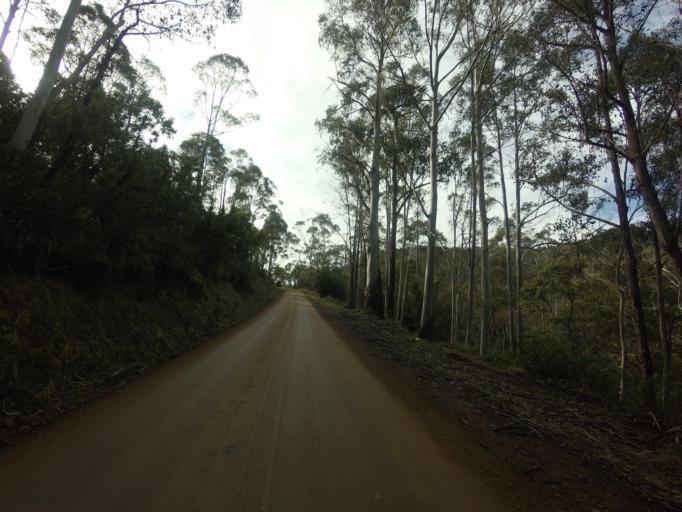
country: AU
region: Tasmania
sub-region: Derwent Valley
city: New Norfolk
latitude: -42.7886
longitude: 146.9416
